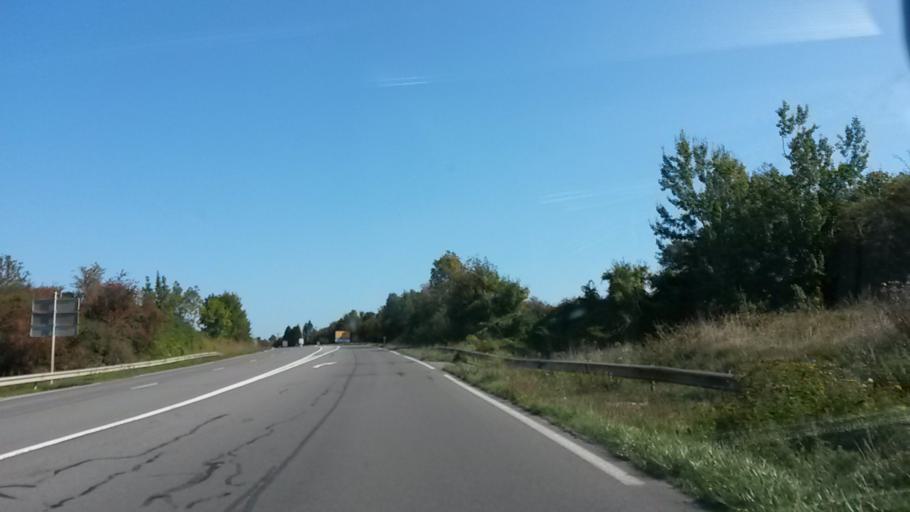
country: FR
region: Picardie
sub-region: Departement de l'Aisne
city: La Flamengrie
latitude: 50.0545
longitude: 3.9315
